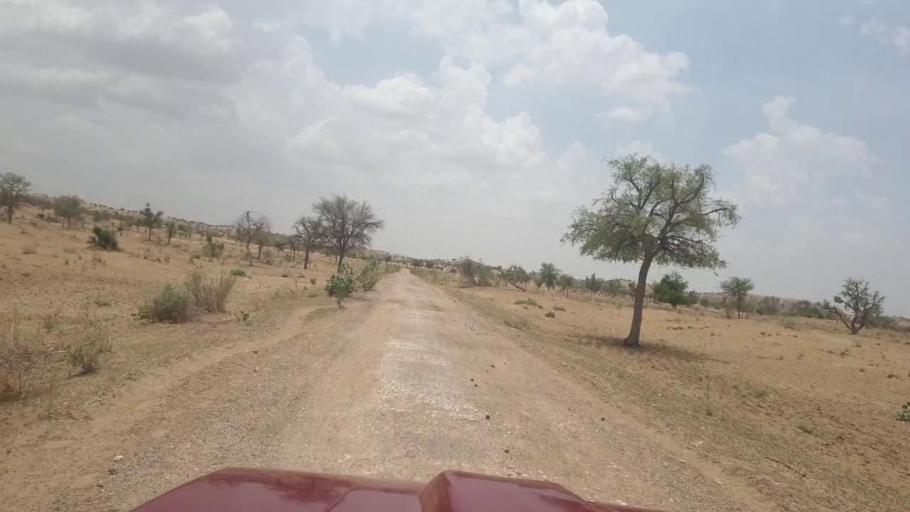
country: PK
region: Sindh
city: Islamkot
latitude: 25.1952
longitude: 70.4309
